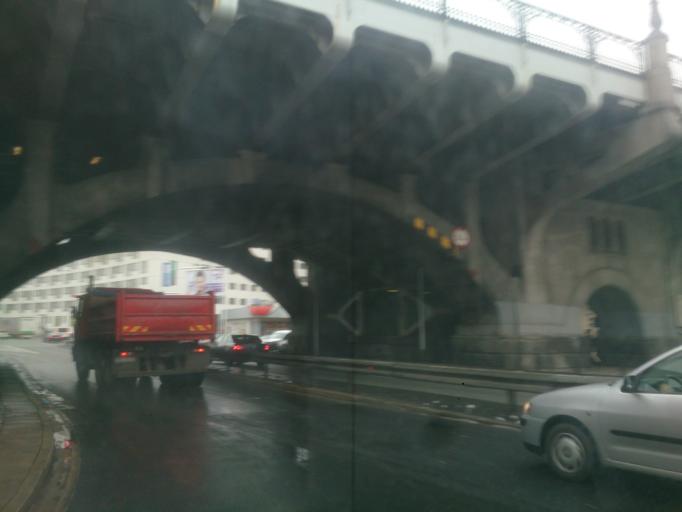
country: PL
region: Masovian Voivodeship
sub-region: Warszawa
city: Praga Polnoc
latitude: 52.2352
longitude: 21.0363
